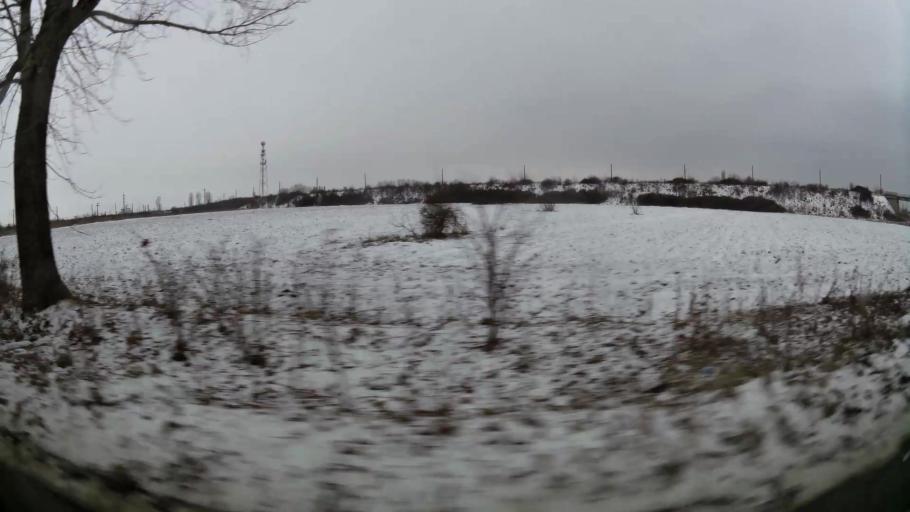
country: RO
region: Prahova
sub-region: Comuna Berceni
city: Corlatesti
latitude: 44.9311
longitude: 26.0626
